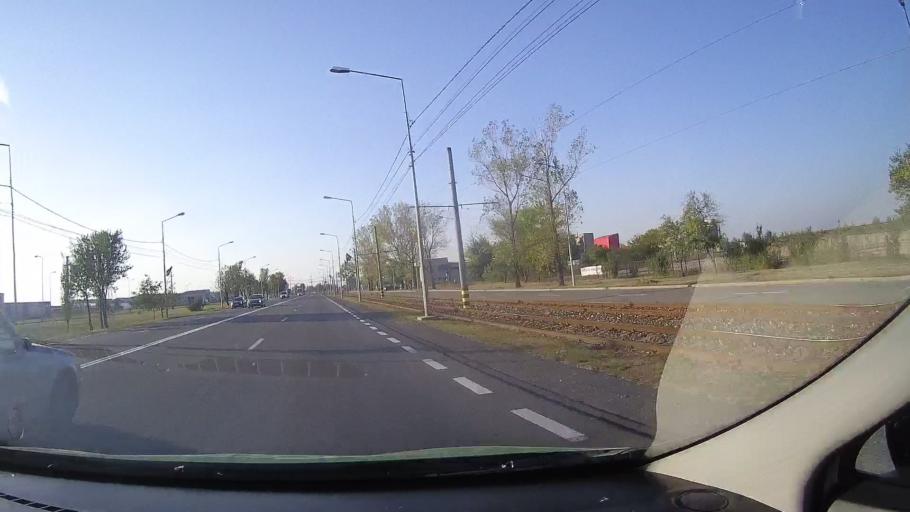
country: RO
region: Bihor
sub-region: Comuna Santandrei
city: Santandrei
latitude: 47.0836
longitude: 21.8867
